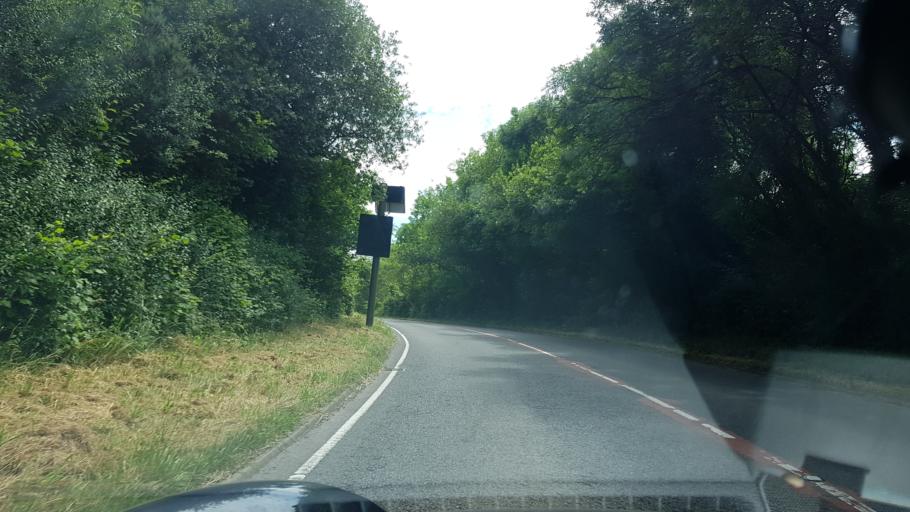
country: GB
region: Wales
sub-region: Carmarthenshire
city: Saint Clears
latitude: 51.8043
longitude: -4.4965
